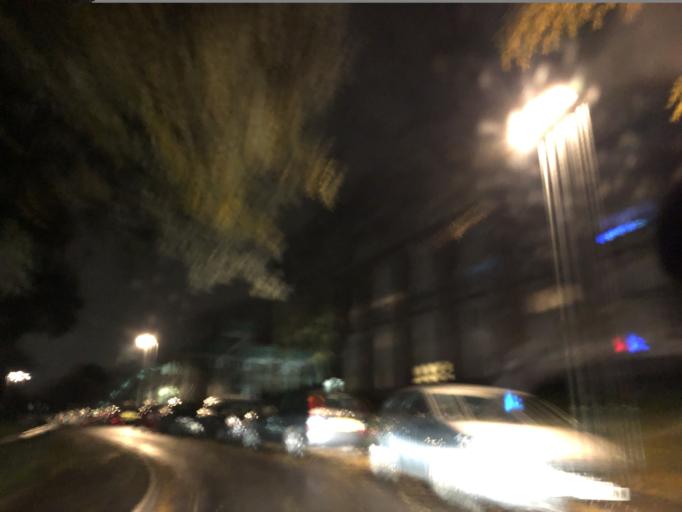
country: GB
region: England
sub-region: Borough of Oldham
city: Shaw
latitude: 53.5496
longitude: -2.0828
